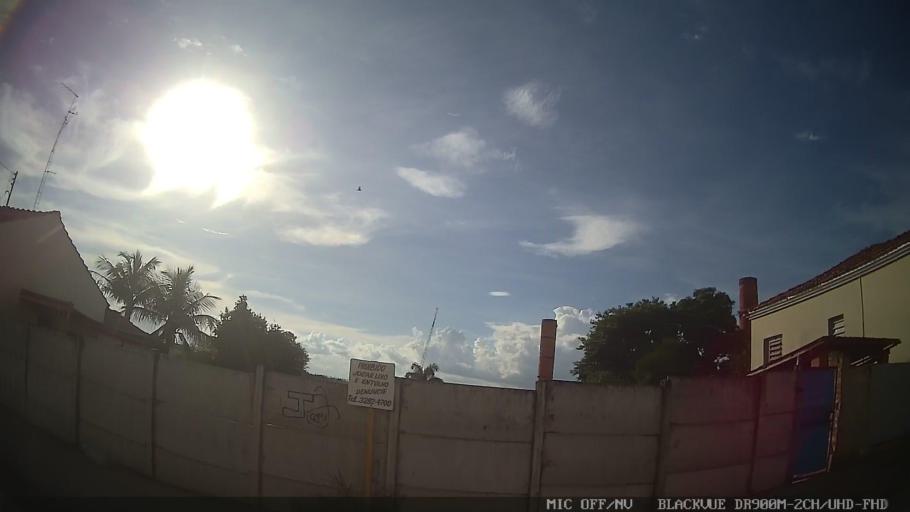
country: BR
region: Sao Paulo
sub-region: Tiete
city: Tiete
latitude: -23.1076
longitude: -47.7158
